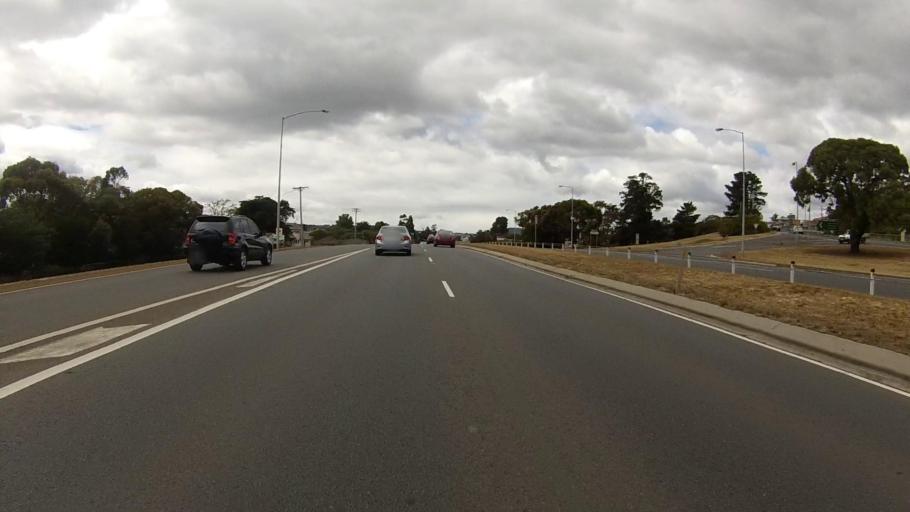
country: AU
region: Tasmania
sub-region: Glenorchy
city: Berriedale
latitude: -42.8178
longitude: 147.2602
